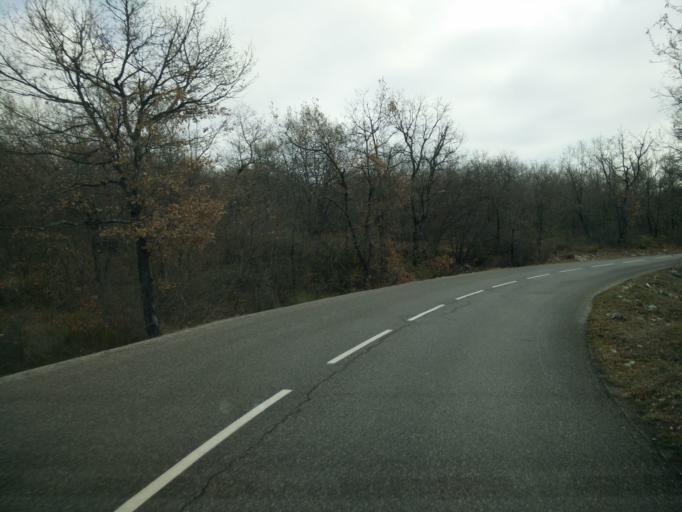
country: FR
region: Provence-Alpes-Cote d'Azur
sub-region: Departement des Alpes-Maritimes
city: Le Broc
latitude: 43.8250
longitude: 7.1533
